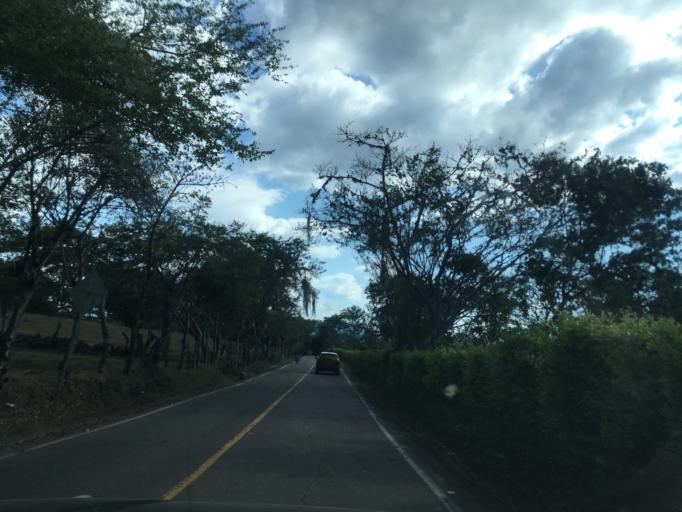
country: CO
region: Santander
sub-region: San Gil
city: San Gil
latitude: 6.5862
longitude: -73.1578
